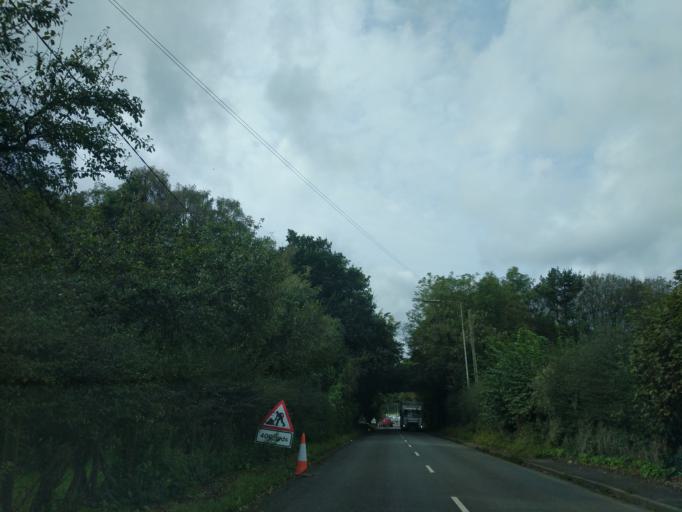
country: GB
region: England
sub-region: Staffordshire
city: Audley
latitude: 53.0092
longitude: -2.3070
